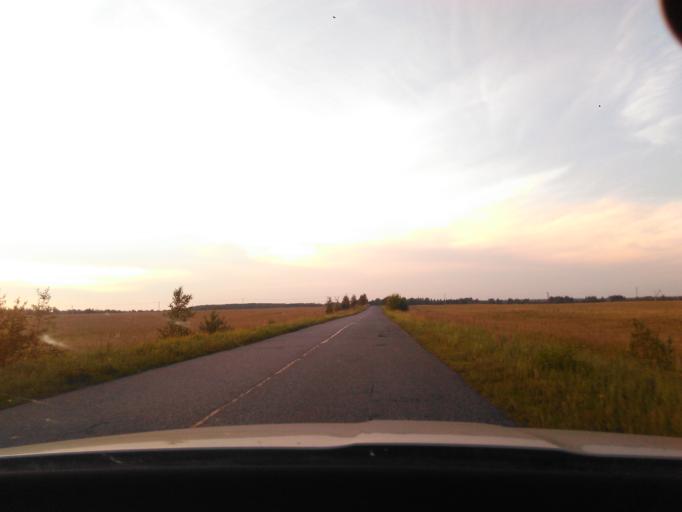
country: RU
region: Tverskaya
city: Zavidovo
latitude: 56.5988
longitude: 36.5994
